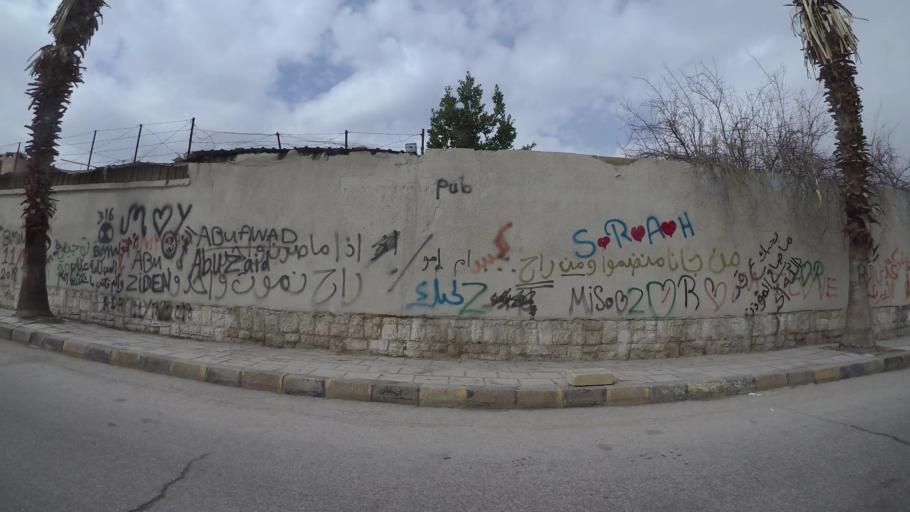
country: JO
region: Amman
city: Amman
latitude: 31.9707
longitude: 35.9345
